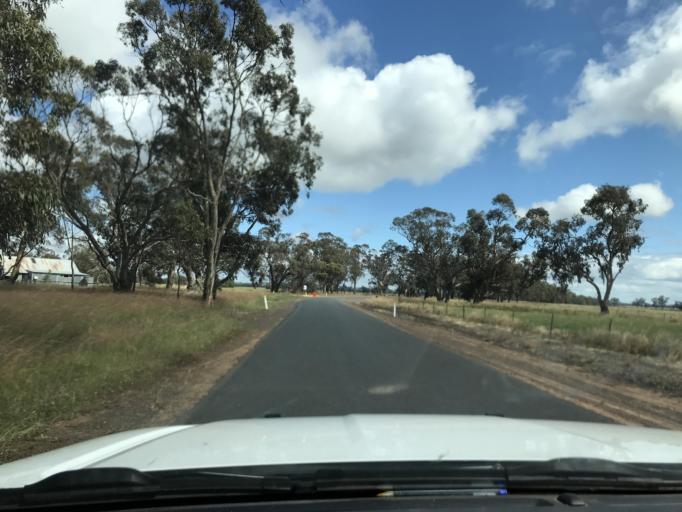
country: AU
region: Victoria
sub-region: Horsham
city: Horsham
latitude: -36.8066
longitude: 141.4790
